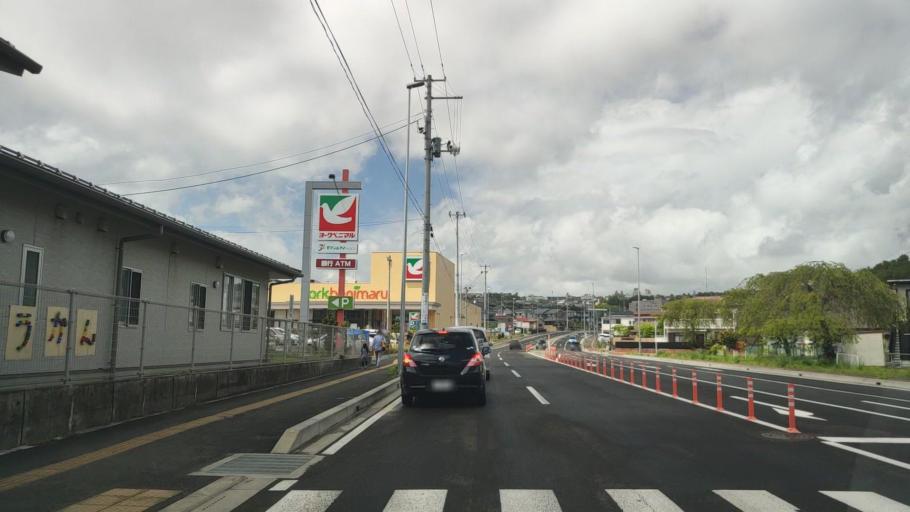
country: JP
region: Miyagi
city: Sendai
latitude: 38.2308
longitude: 140.8553
